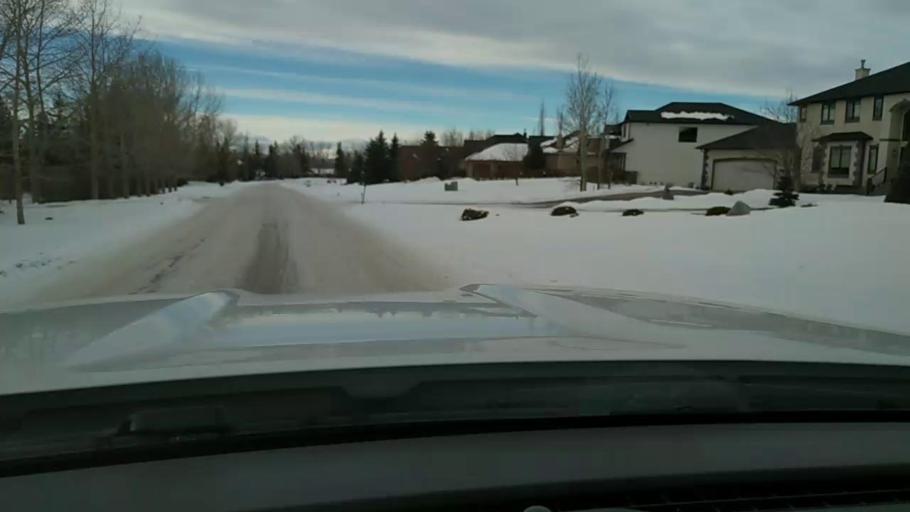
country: CA
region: Alberta
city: Calgary
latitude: 51.1169
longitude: -114.2622
